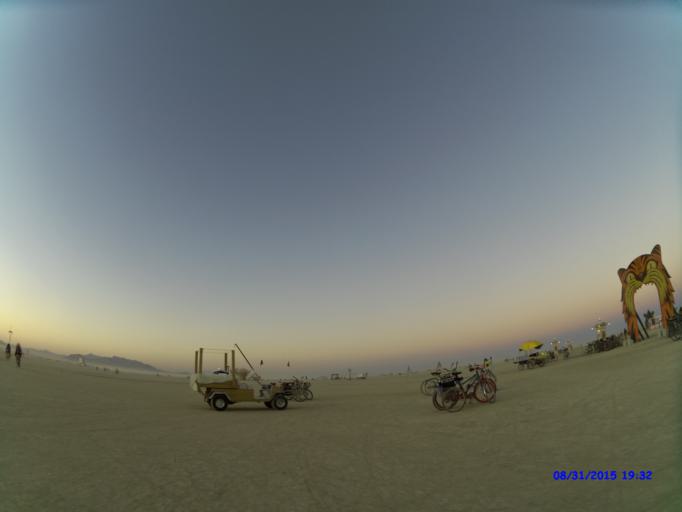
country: US
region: Nevada
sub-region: Pershing County
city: Lovelock
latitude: 40.7869
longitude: -119.2075
